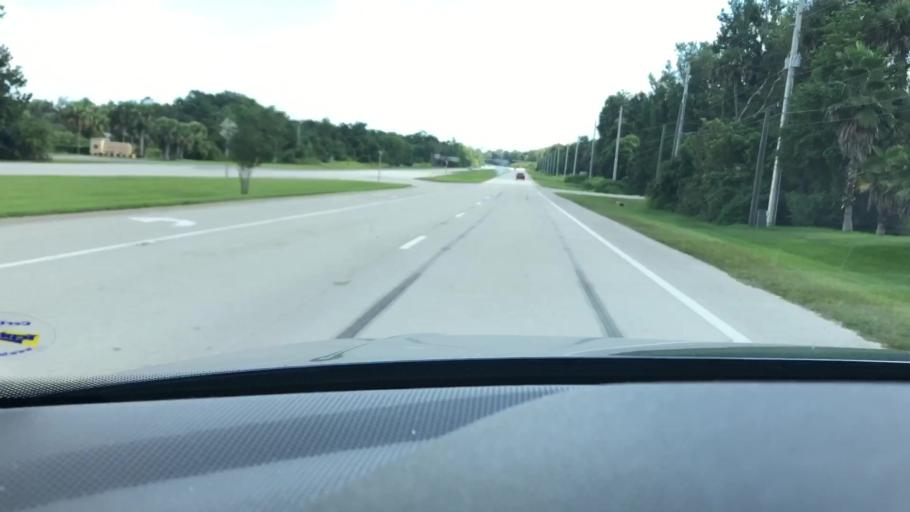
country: US
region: Florida
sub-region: Volusia County
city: Edgewater
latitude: 28.9516
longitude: -80.9433
